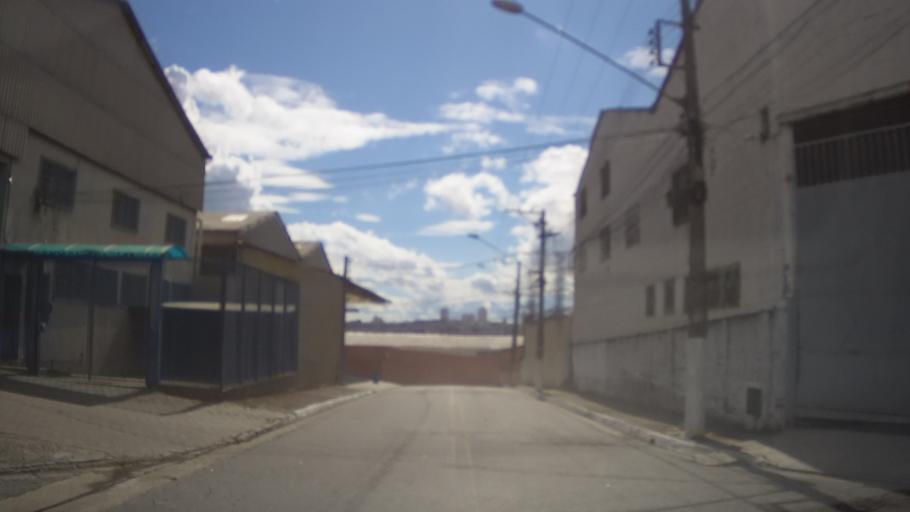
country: BR
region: Sao Paulo
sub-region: Guarulhos
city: Guarulhos
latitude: -23.4875
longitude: -46.5556
